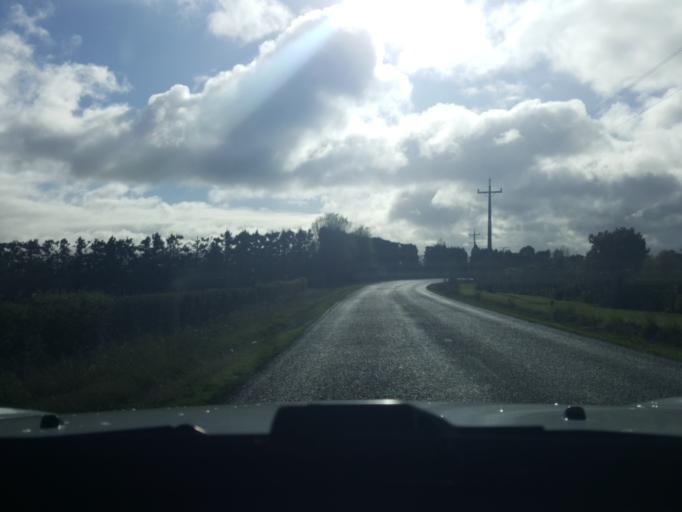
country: NZ
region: Auckland
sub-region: Auckland
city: Pukekohe East
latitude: -37.3055
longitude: 175.0129
